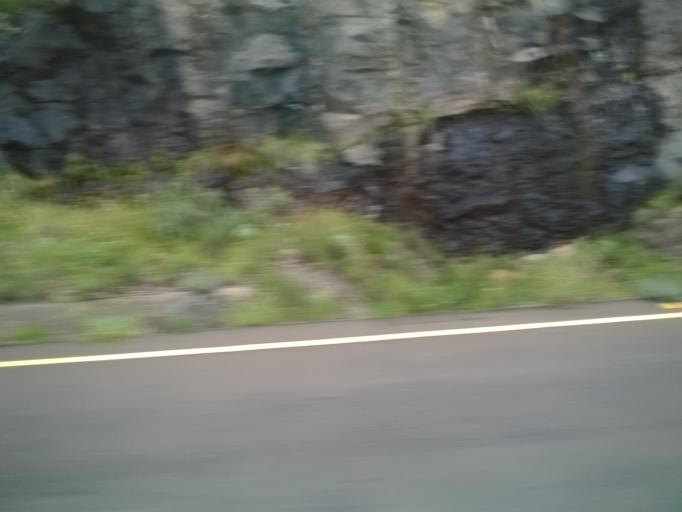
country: LS
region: Butha-Buthe
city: Butha-Buthe
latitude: -29.0689
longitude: 28.3928
